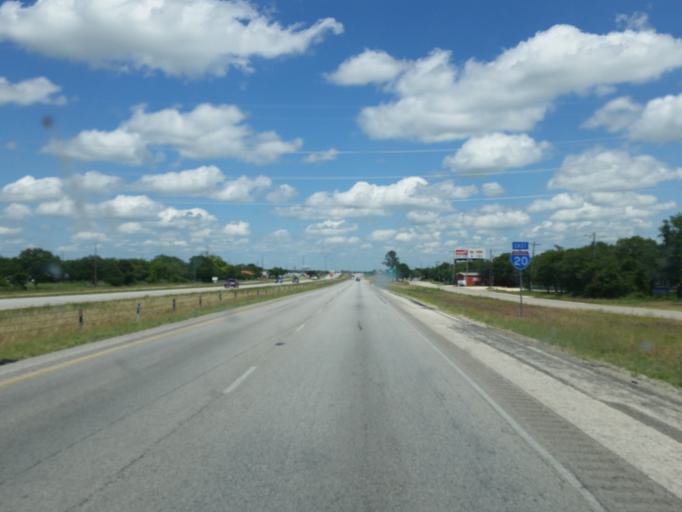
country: US
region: Texas
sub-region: Callahan County
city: Clyde
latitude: 32.4168
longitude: -99.5177
